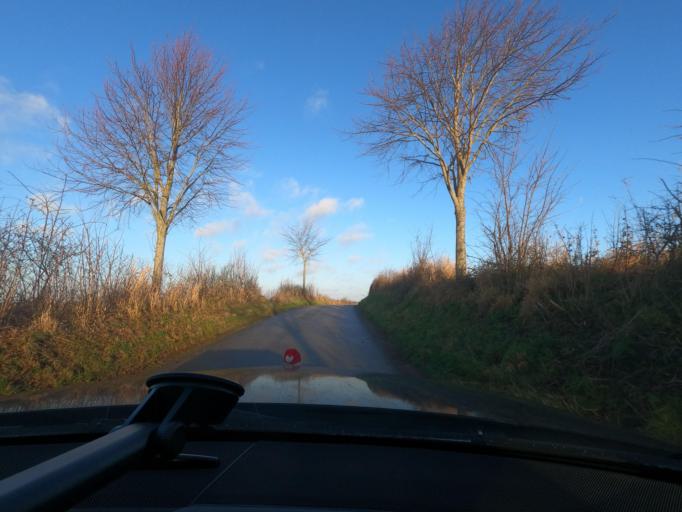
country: DK
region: South Denmark
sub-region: Sonderborg Kommune
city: Broager
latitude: 54.8924
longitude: 9.6893
